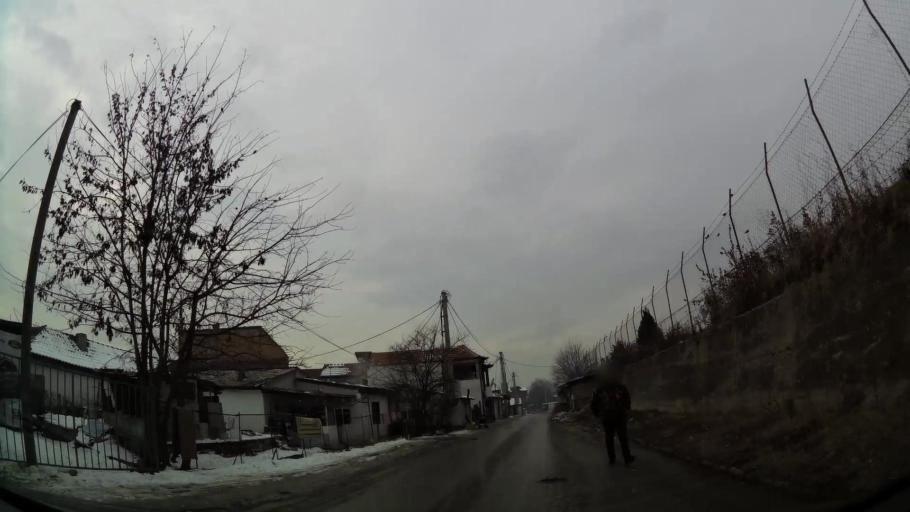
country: MK
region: Suto Orizari
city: Suto Orizare
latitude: 42.0454
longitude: 21.4264
